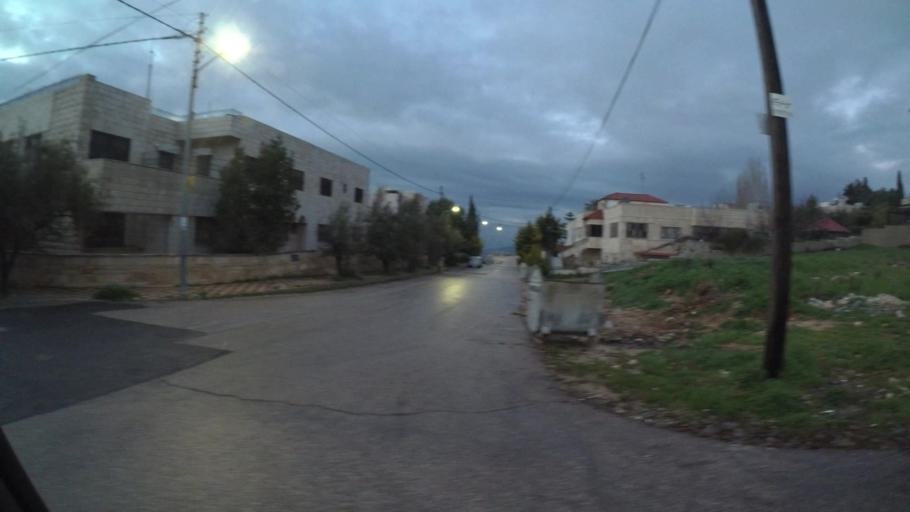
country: JO
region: Amman
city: Al Jubayhah
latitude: 32.0308
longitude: 35.8131
